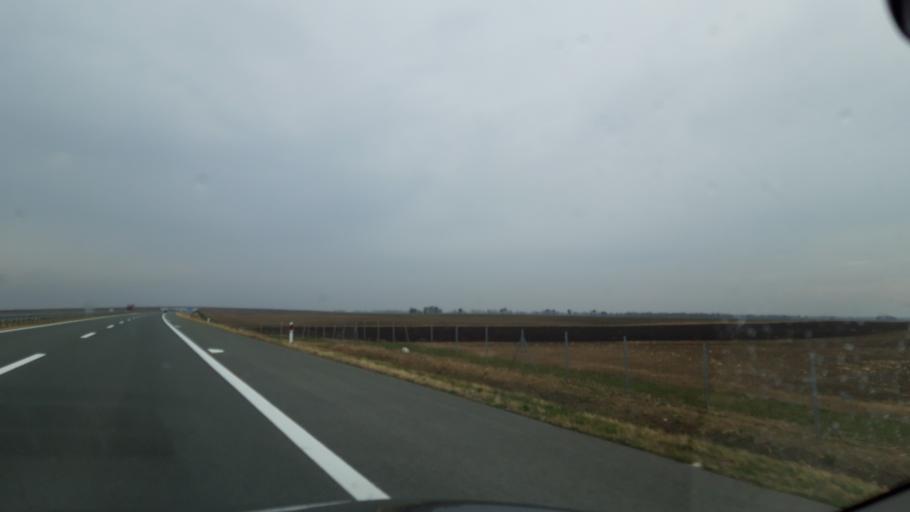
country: RS
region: Autonomna Pokrajina Vojvodina
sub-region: Severnobacki Okrug
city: Mali Igos
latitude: 45.7390
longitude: 19.7035
